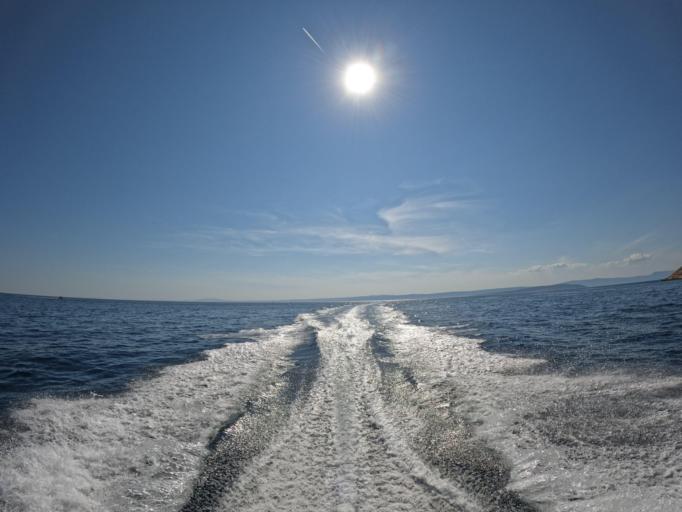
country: HR
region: Primorsko-Goranska
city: Punat
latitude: 44.9624
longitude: 14.6556
